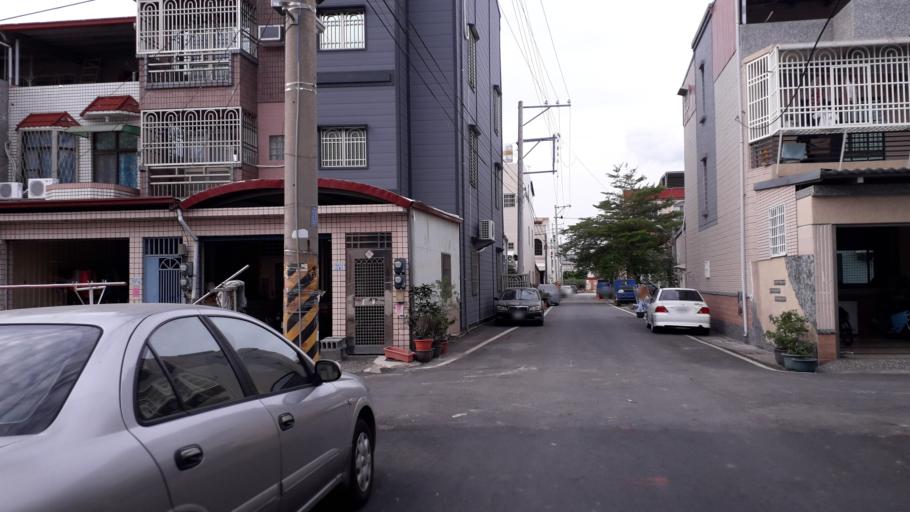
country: TW
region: Taiwan
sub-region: Pingtung
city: Pingtung
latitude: 22.3644
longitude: 120.6025
